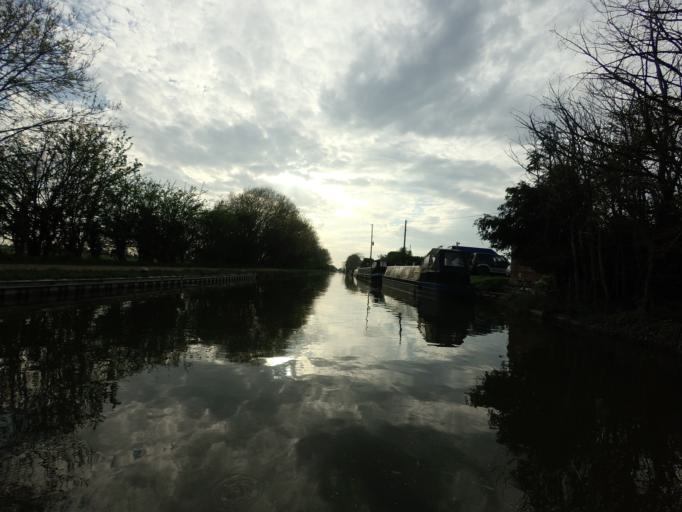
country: GB
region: England
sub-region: Buckinghamshire
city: Aston Clinton
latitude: 51.8176
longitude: -0.7365
